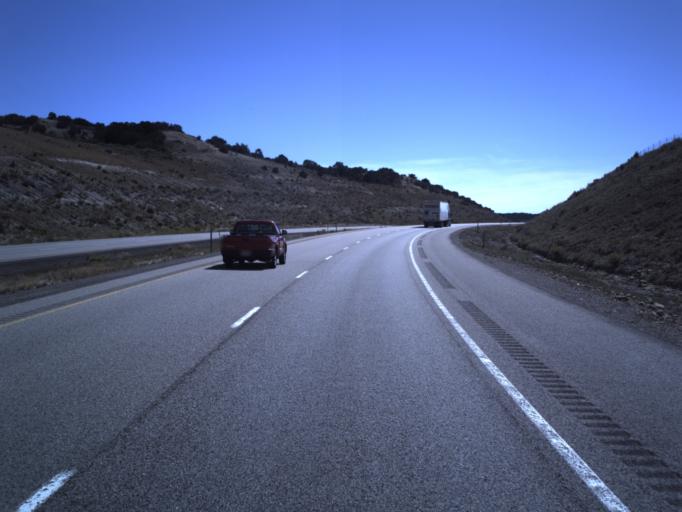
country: US
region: Utah
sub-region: Wayne County
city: Loa
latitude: 38.7826
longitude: -111.4888
